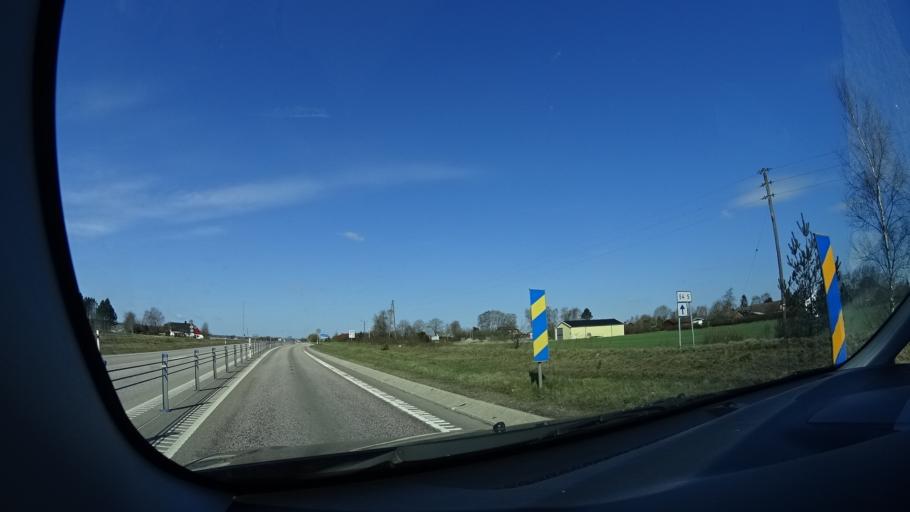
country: SE
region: Skane
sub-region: Astorps Kommun
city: Kvidinge
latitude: 56.1281
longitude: 13.0599
